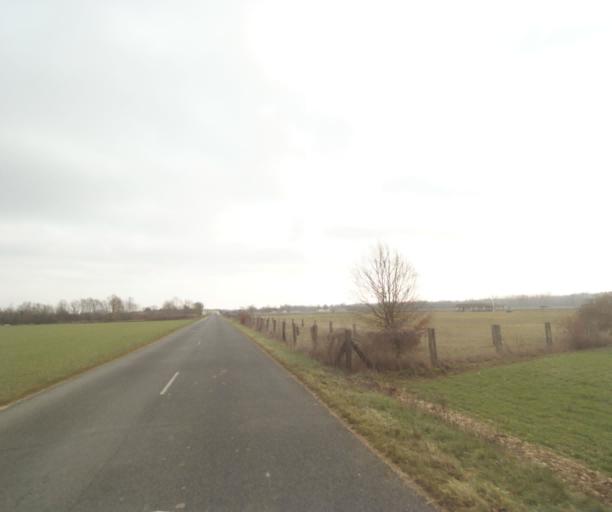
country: FR
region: Champagne-Ardenne
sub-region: Departement de la Haute-Marne
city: Villiers-en-Lieu
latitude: 48.6521
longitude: 4.8024
